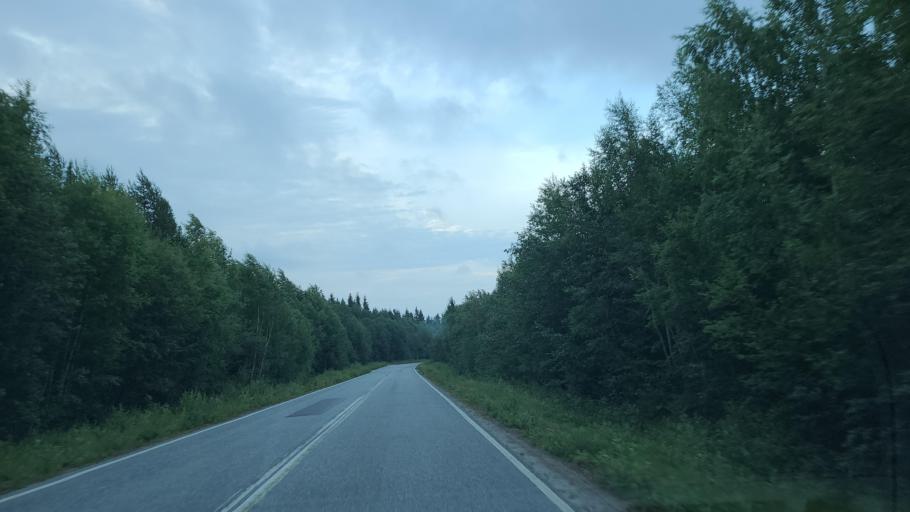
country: FI
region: Ostrobothnia
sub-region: Vaasa
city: Replot
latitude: 63.2731
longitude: 21.1556
